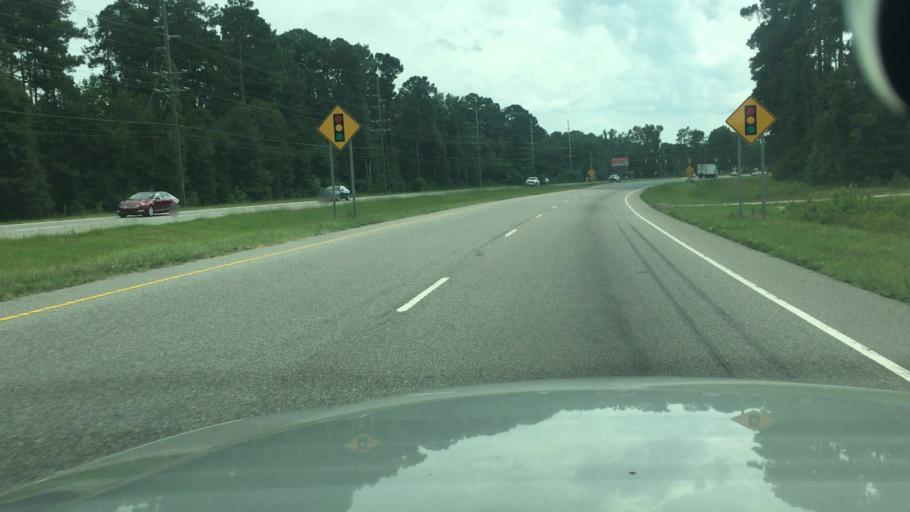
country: US
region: North Carolina
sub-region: Cumberland County
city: Vander
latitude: 34.9524
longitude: -78.8444
